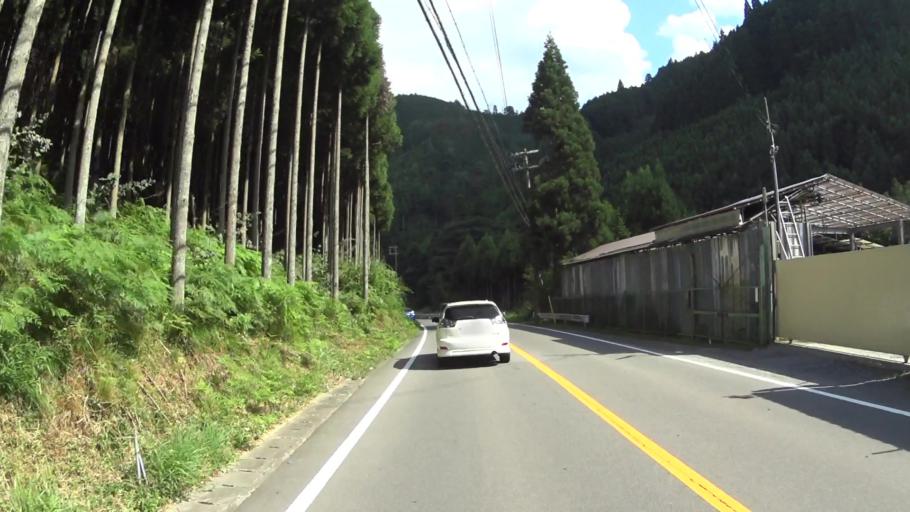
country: JP
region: Kyoto
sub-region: Kyoto-shi
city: Kamigyo-ku
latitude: 35.0987
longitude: 135.6769
